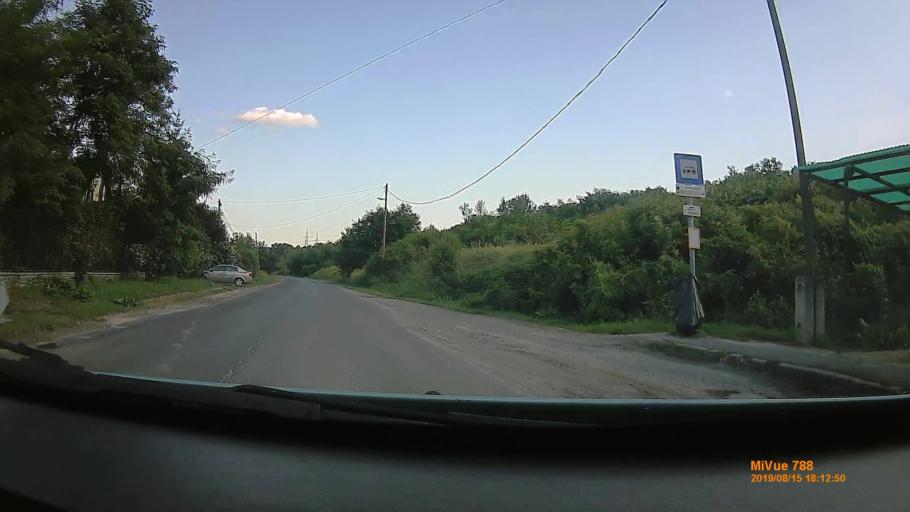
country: HU
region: Borsod-Abauj-Zemplen
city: Sajobabony
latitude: 48.1120
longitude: 20.7181
